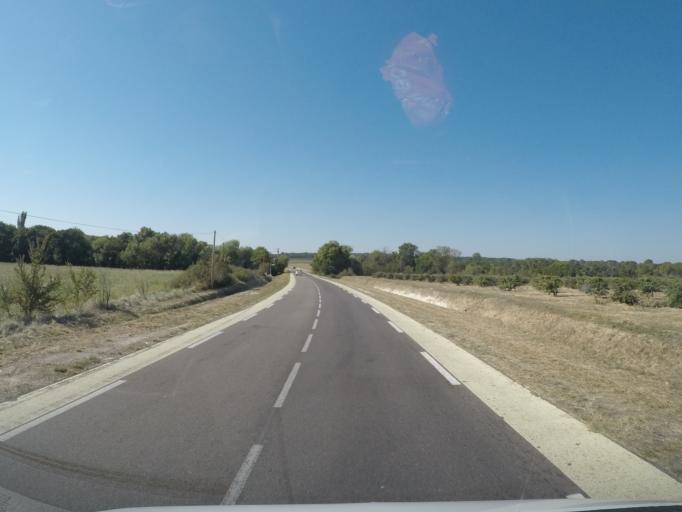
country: FR
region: Languedoc-Roussillon
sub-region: Departement du Gard
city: Uzes
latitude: 43.9992
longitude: 4.3968
